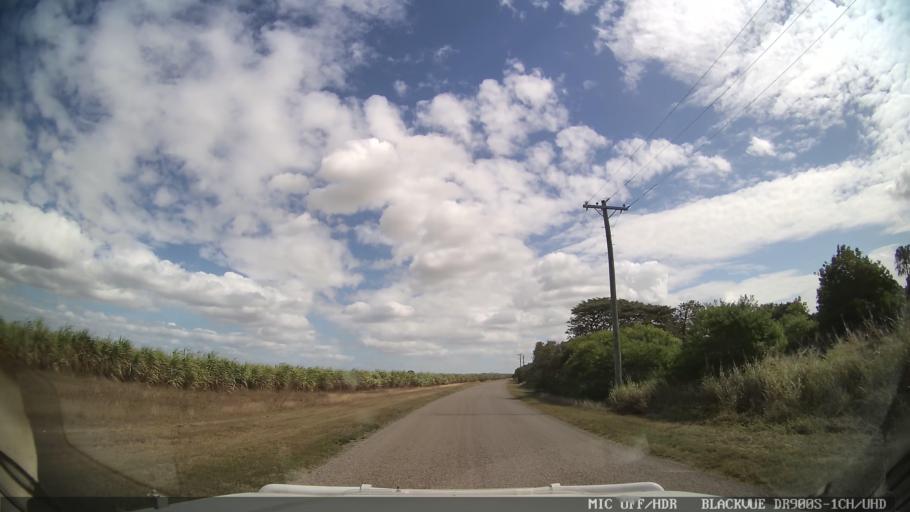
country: AU
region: Queensland
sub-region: Burdekin
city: Home Hill
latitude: -19.7095
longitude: 147.4630
